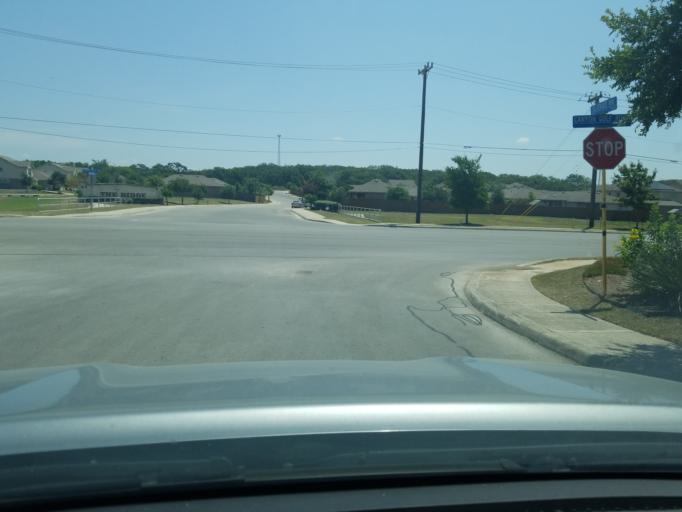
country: US
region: Texas
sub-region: Bexar County
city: Timberwood Park
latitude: 29.7022
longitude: -98.4821
